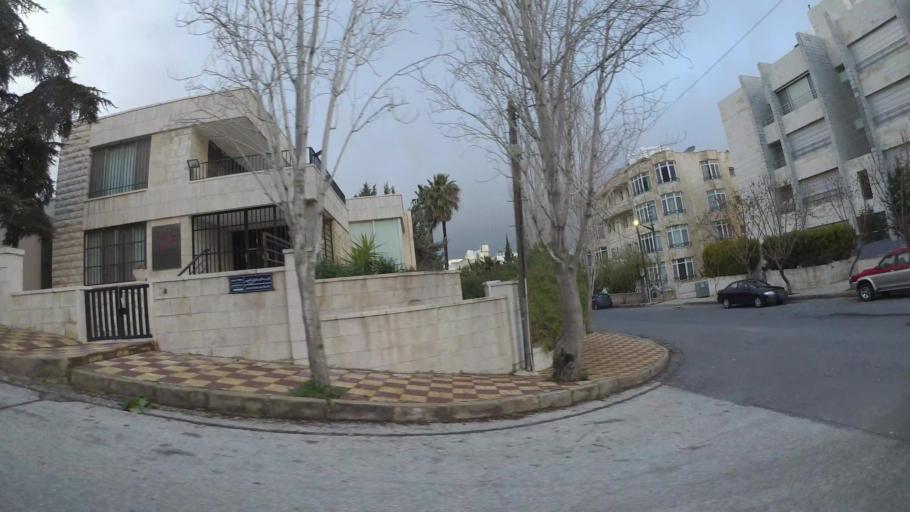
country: JO
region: Amman
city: Amman
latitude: 31.9603
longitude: 35.8880
